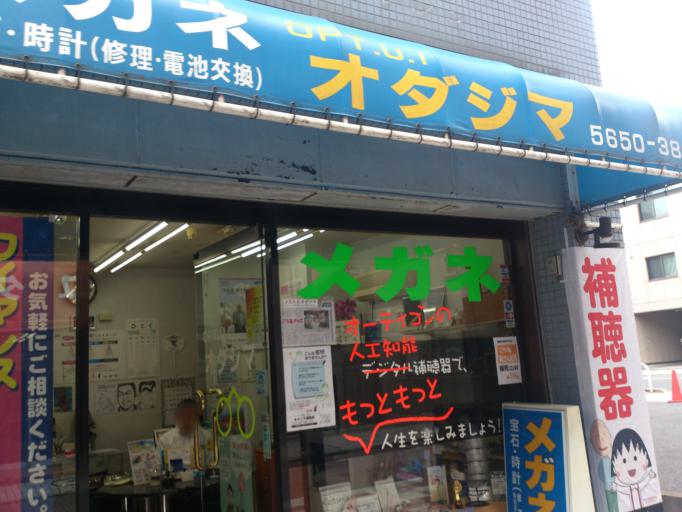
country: JP
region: Chiba
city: Matsudo
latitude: 35.7632
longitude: 139.8492
